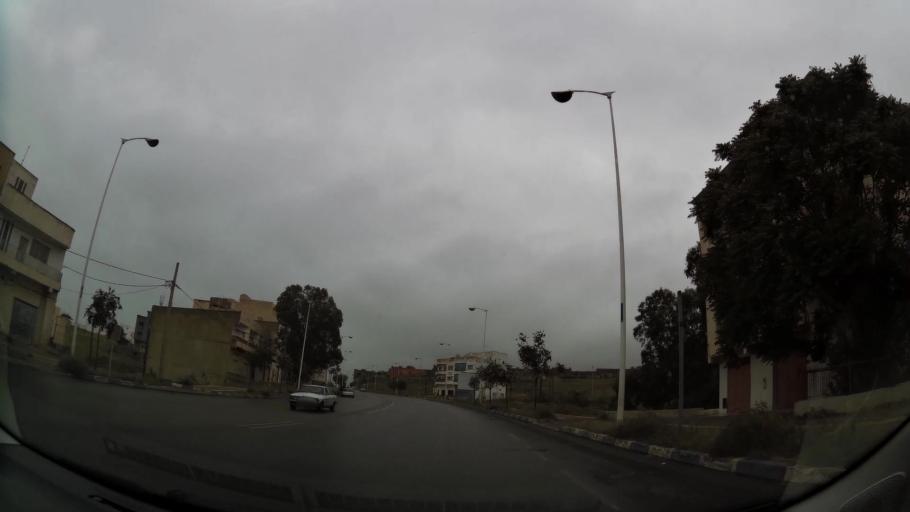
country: MA
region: Oriental
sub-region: Nador
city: Nador
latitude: 35.1907
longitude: -2.9311
